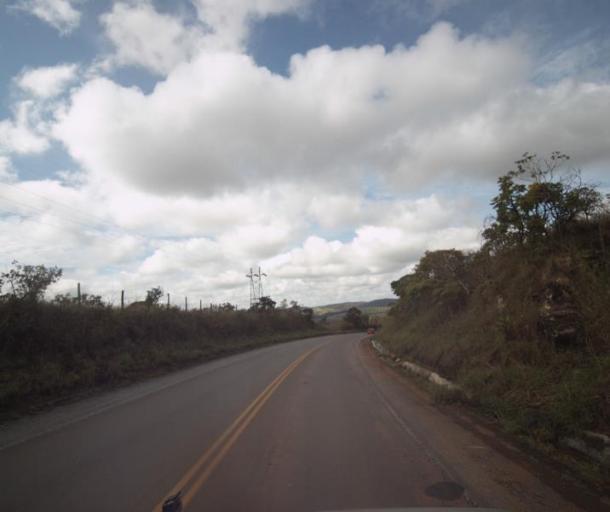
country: BR
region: Goias
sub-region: Pirenopolis
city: Pirenopolis
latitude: -15.8412
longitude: -48.7707
